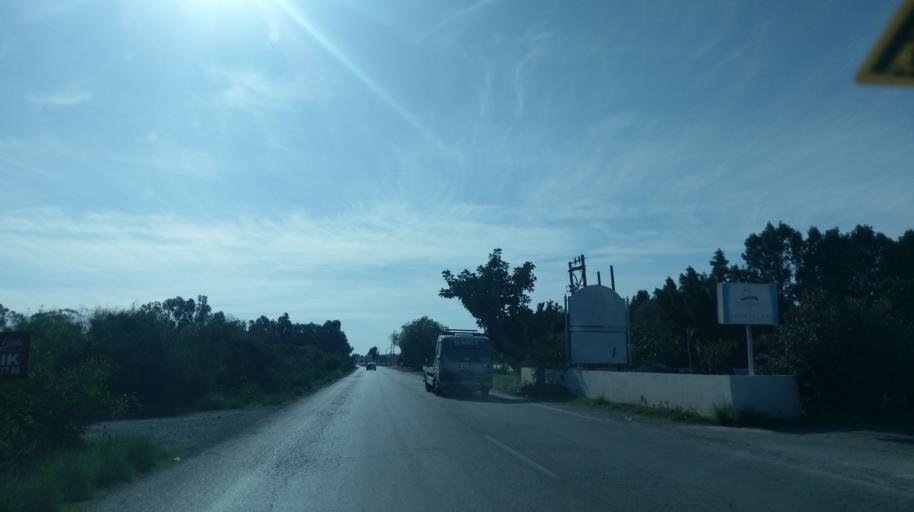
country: CY
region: Ammochostos
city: Trikomo
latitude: 35.2843
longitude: 33.9251
